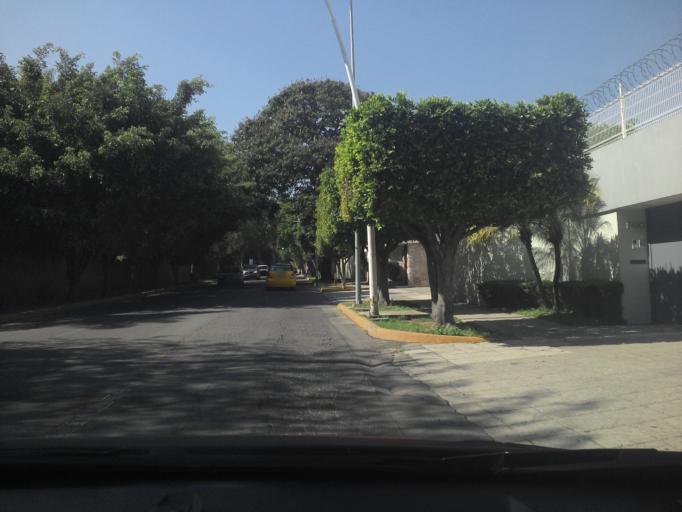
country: MX
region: Jalisco
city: Zapopan2
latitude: 20.6952
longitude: -103.3985
